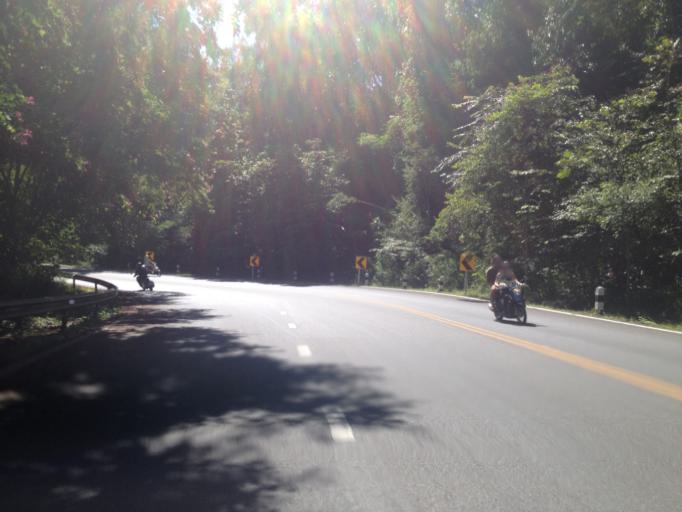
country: TH
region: Chiang Mai
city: Chiang Mai
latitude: 18.8136
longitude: 98.9372
